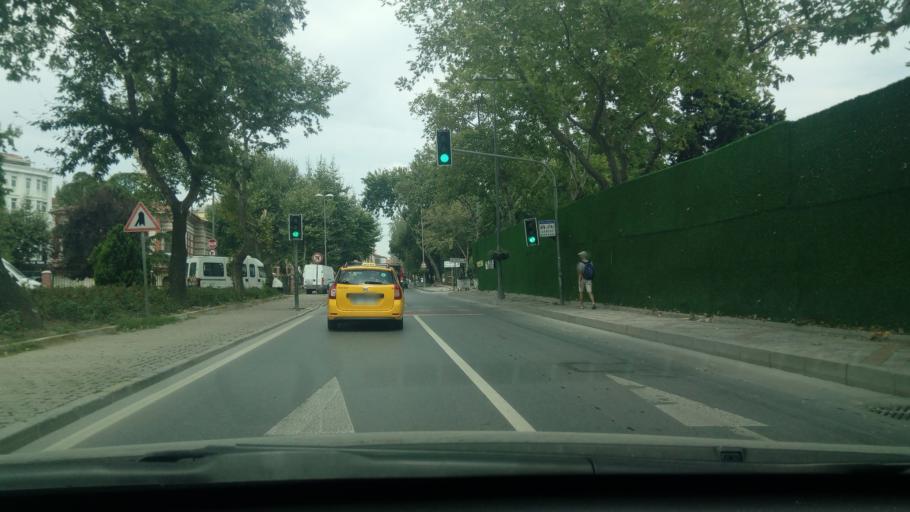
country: TR
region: Istanbul
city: Istanbul
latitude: 41.0341
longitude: 28.9474
